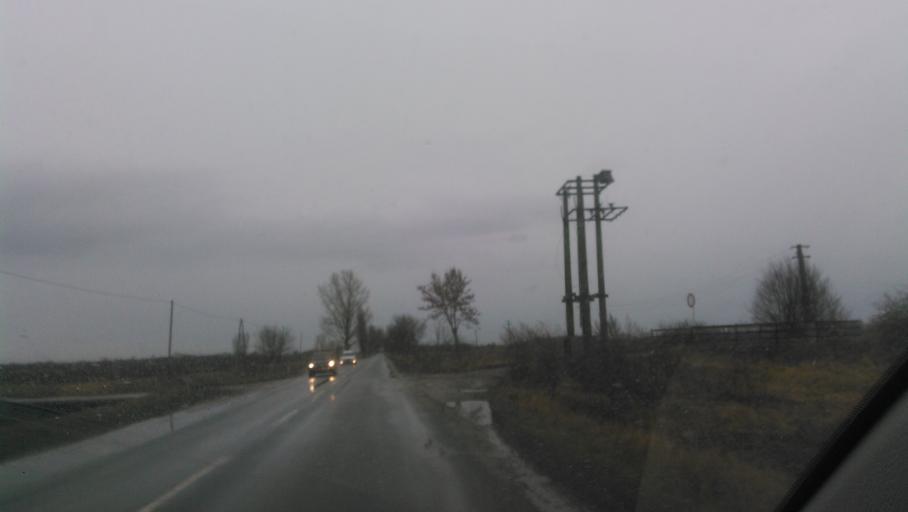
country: SK
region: Nitriansky
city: Sellye
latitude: 48.1349
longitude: 17.8839
